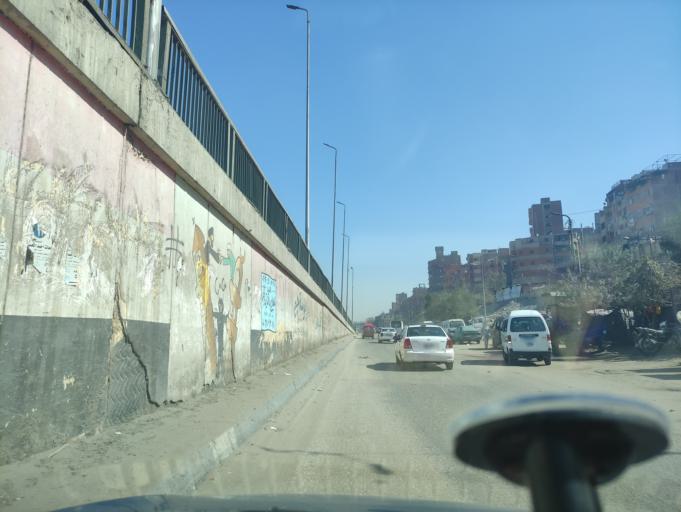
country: EG
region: Muhafazat al Qahirah
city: Cairo
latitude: 30.0387
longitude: 31.2726
